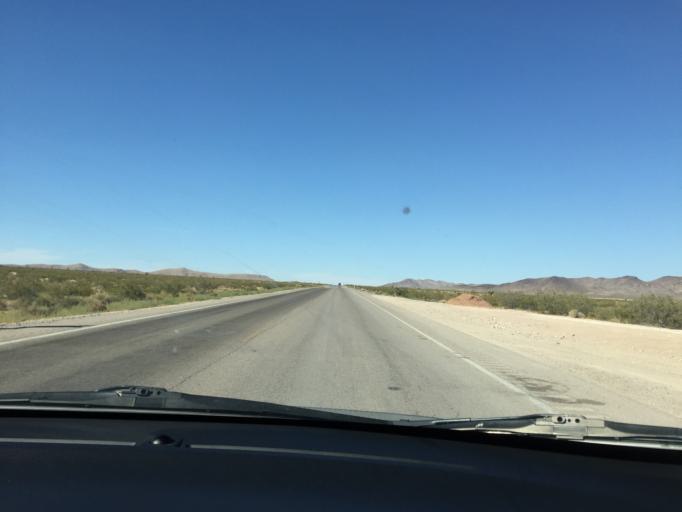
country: US
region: Nevada
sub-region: Clark County
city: Enterprise
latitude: 35.8277
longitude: -115.2838
